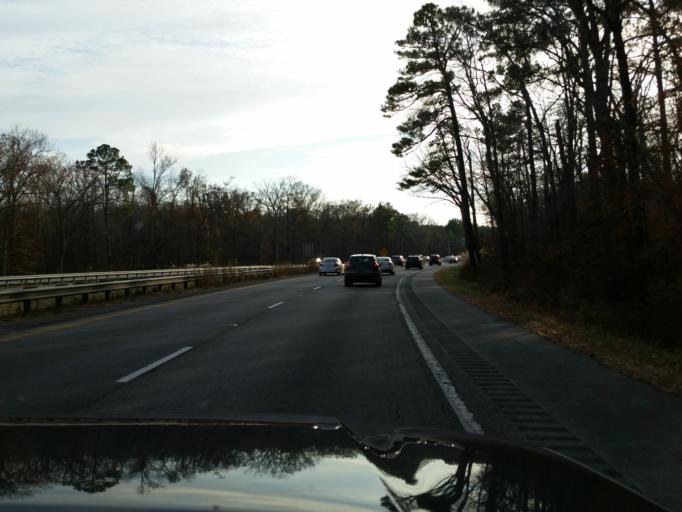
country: US
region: Maryland
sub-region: Queen Anne's County
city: Grasonville
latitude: 38.9774
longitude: -76.1731
